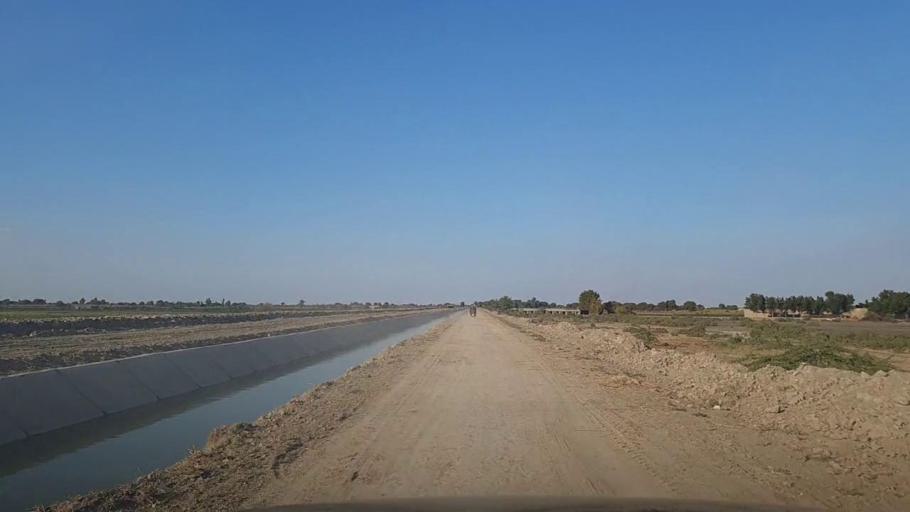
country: PK
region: Sindh
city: Jhol
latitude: 25.8882
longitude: 69.0379
